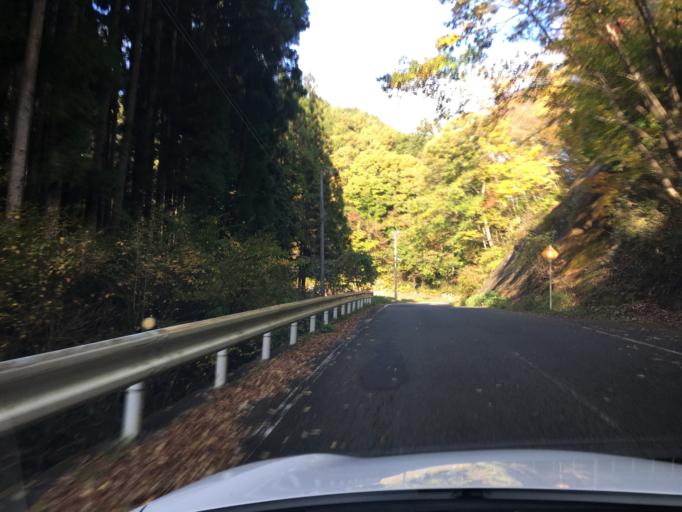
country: JP
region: Fukushima
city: Iwaki
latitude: 37.2279
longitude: 140.7574
